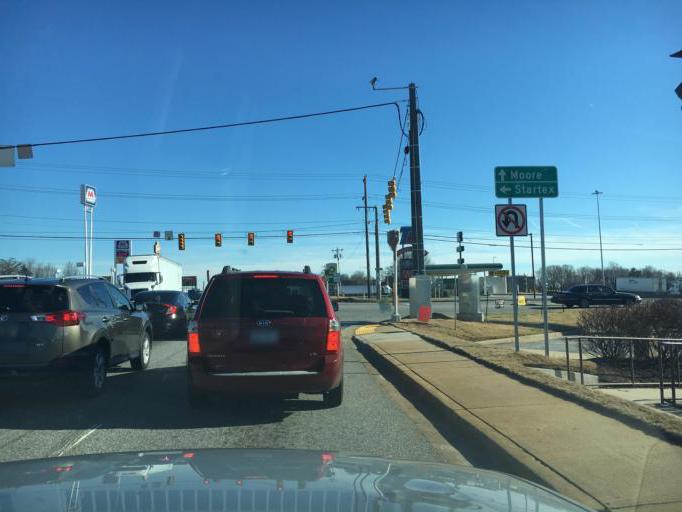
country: US
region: South Carolina
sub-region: Spartanburg County
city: Wellford
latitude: 34.9164
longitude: -82.1105
